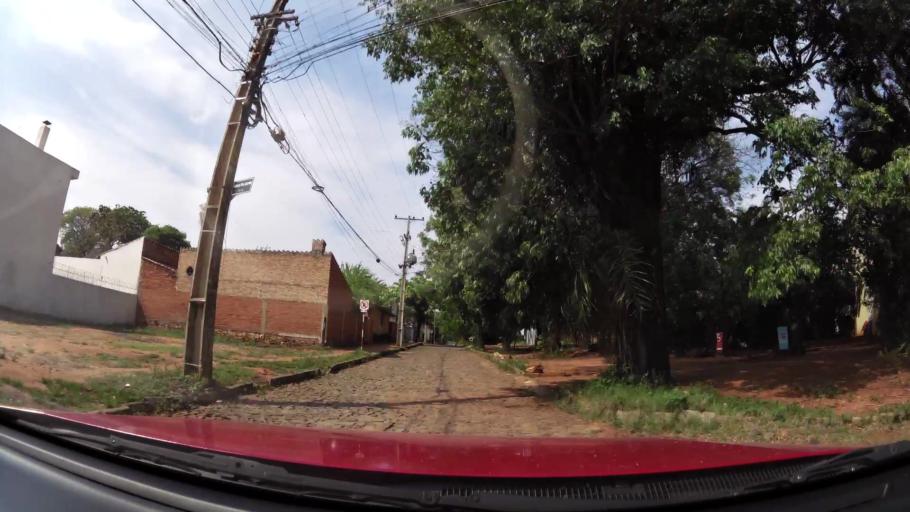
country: PY
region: Asuncion
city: Asuncion
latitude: -25.2634
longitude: -57.5679
